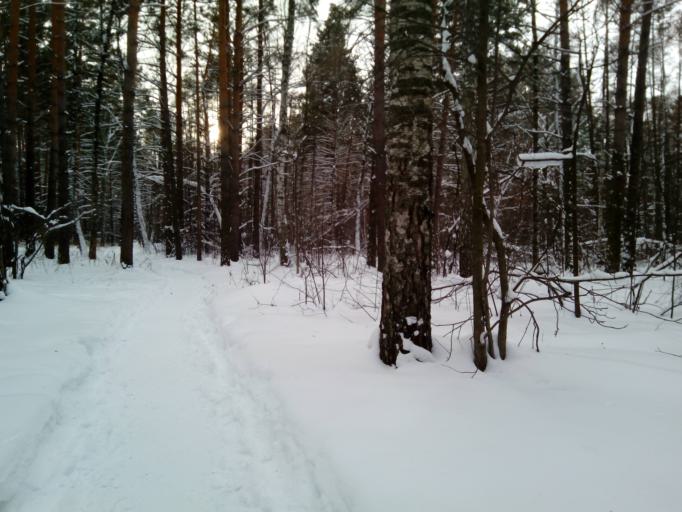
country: RU
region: Novosibirsk
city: Akademgorodok
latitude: 54.8580
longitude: 83.0928
